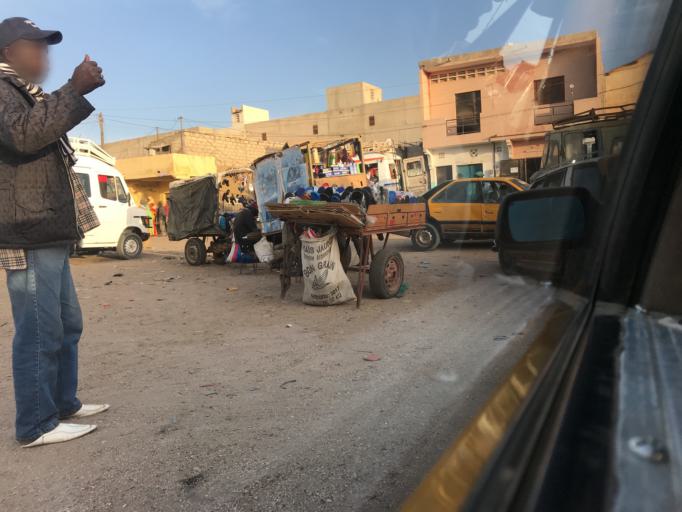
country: SN
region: Saint-Louis
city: Saint-Louis
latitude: 16.0218
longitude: -16.4918
